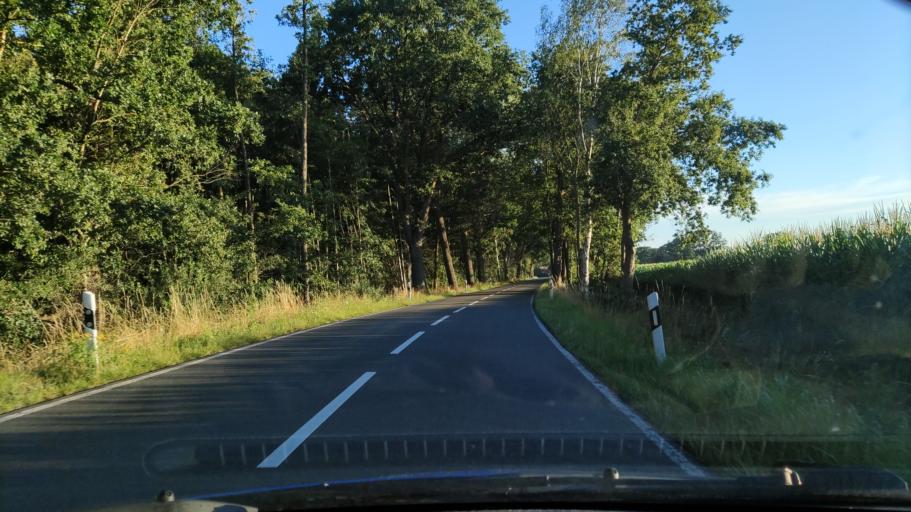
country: DE
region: Lower Saxony
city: Jameln
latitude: 53.0323
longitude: 11.1296
